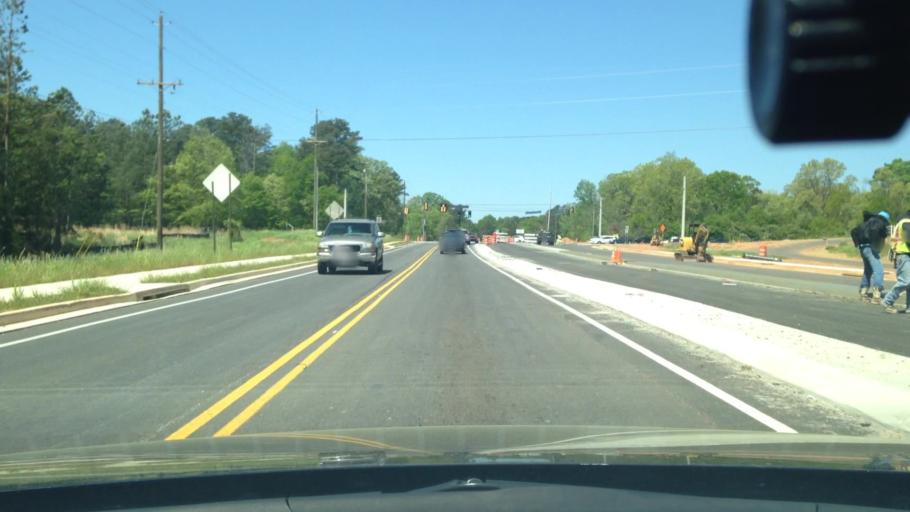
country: US
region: Georgia
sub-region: Coweta County
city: East Newnan
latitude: 33.3606
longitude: -84.7638
